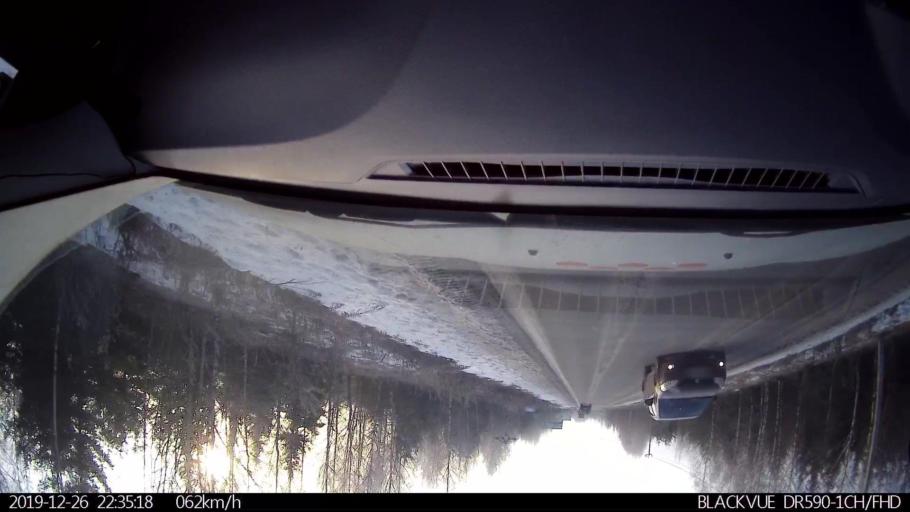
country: RU
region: Nizjnij Novgorod
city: Burevestnik
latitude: 56.1485
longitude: 43.7185
